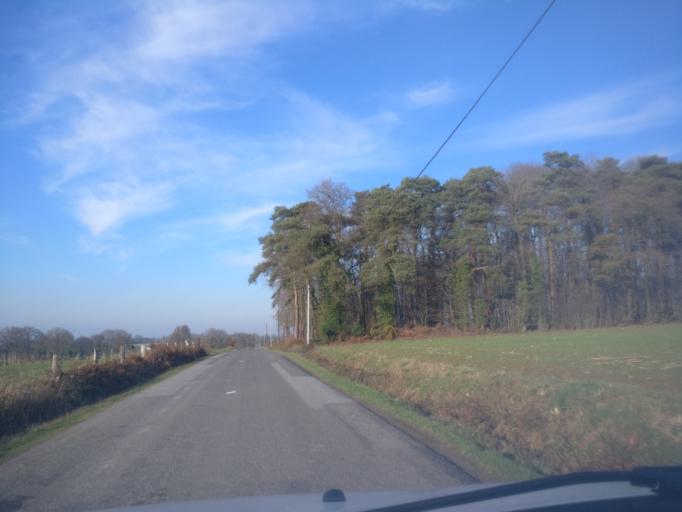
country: FR
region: Brittany
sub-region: Departement d'Ille-et-Vilaine
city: Livre-sur-Changeon
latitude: 48.1967
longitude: -1.3086
